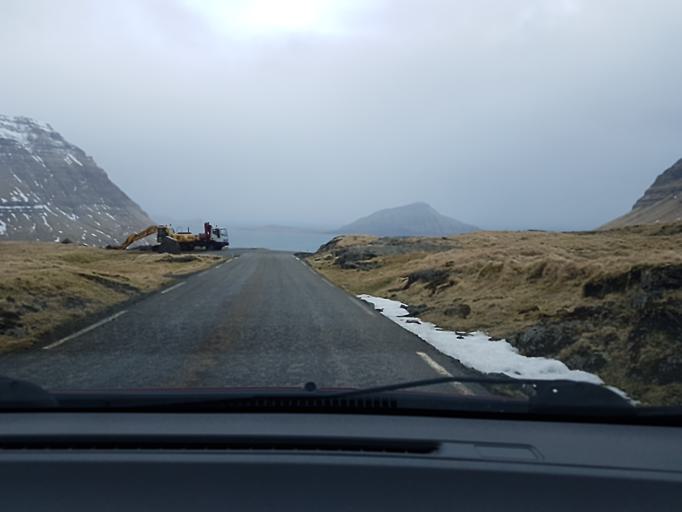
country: FO
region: Streymoy
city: Kollafjordhur
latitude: 62.0514
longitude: -6.9221
